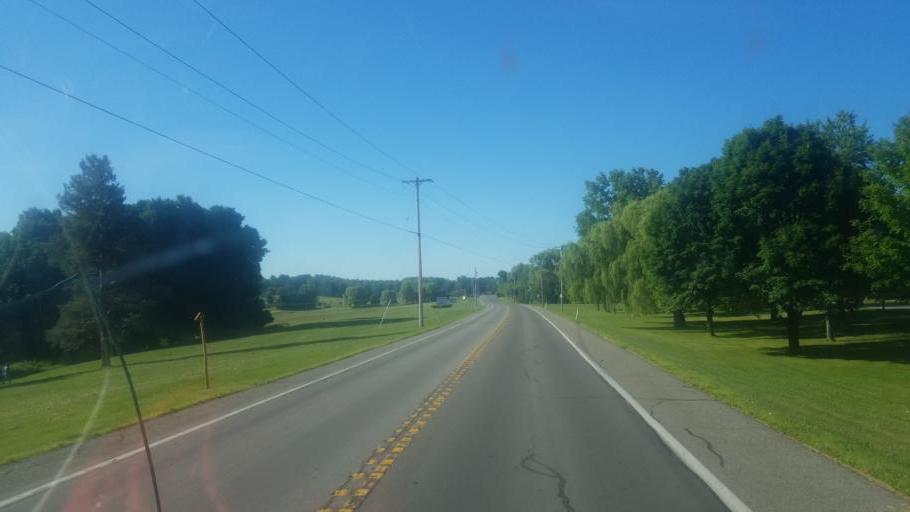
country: US
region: New York
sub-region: Wayne County
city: Newark
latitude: 43.0266
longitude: -77.0960
